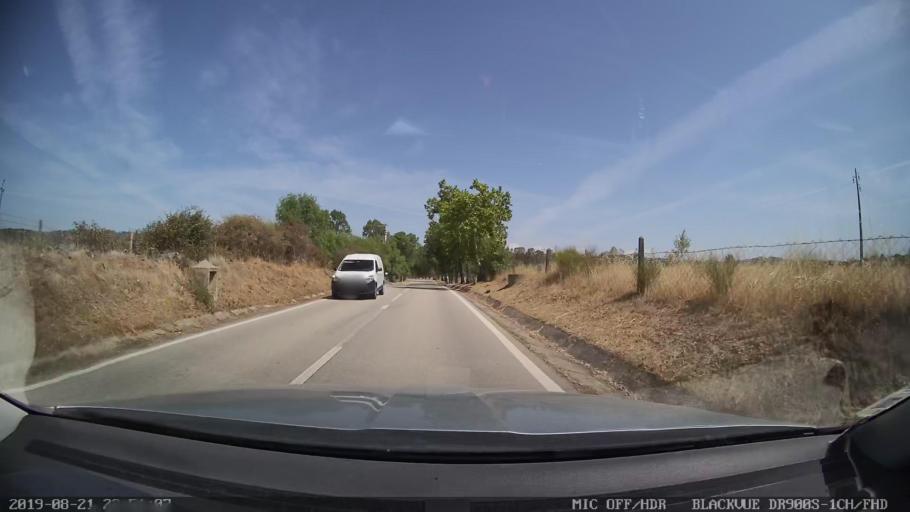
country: PT
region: Castelo Branco
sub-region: Idanha-A-Nova
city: Idanha-a-Nova
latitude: 39.8978
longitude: -7.2356
